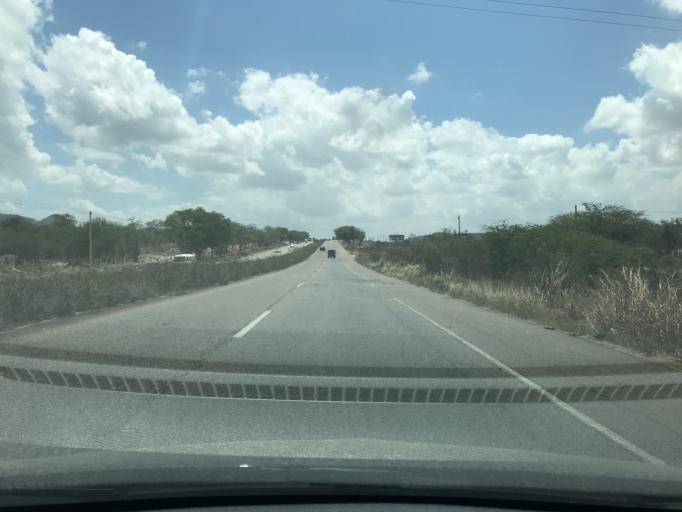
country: BR
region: Pernambuco
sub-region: Bezerros
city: Bezerros
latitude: -8.2977
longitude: -35.8634
